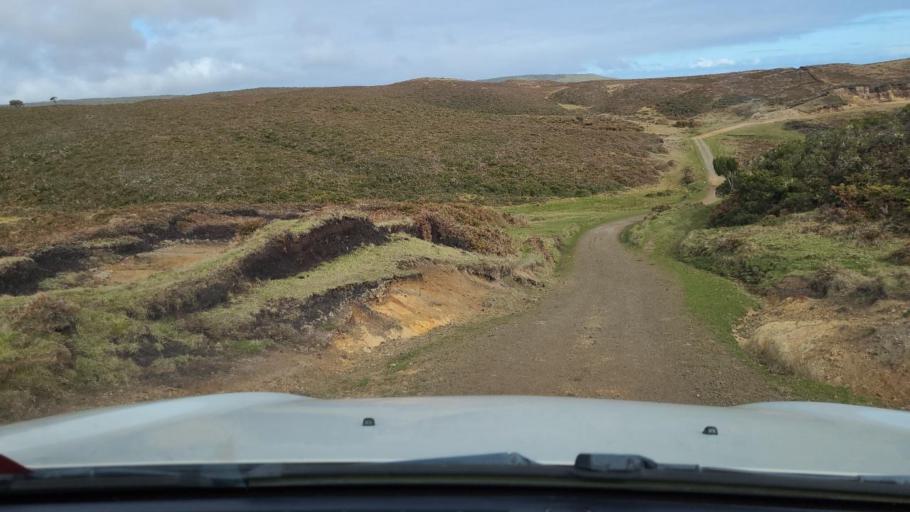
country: NZ
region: Chatham Islands
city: Waitangi
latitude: -44.0556
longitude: -176.6331
